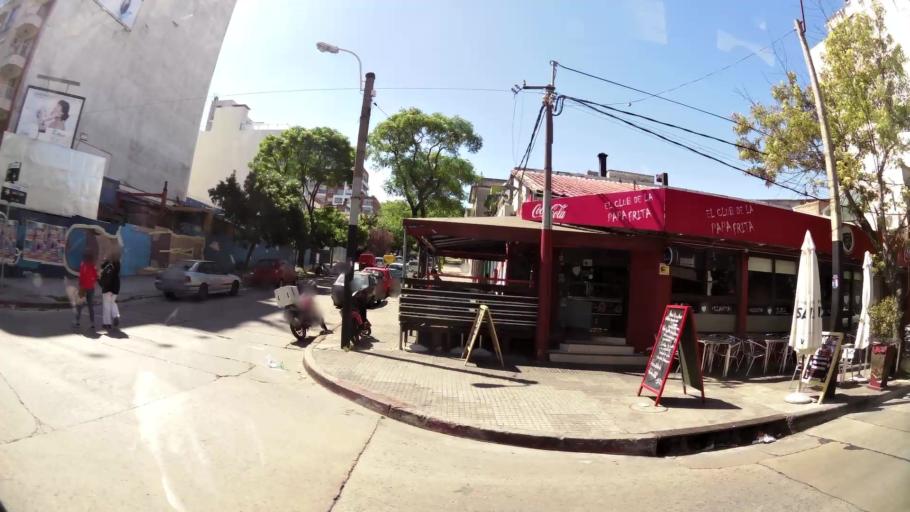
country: UY
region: Montevideo
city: Montevideo
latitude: -34.9068
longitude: -56.1422
